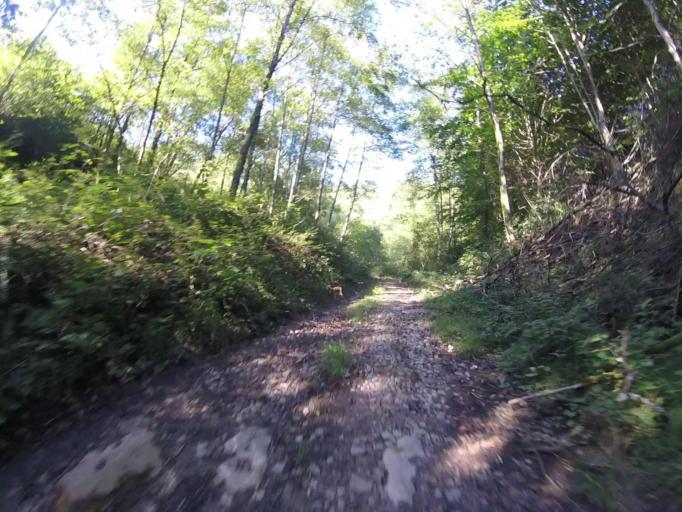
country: ES
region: Navarre
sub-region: Provincia de Navarra
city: Arano
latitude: 43.2484
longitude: -1.9007
